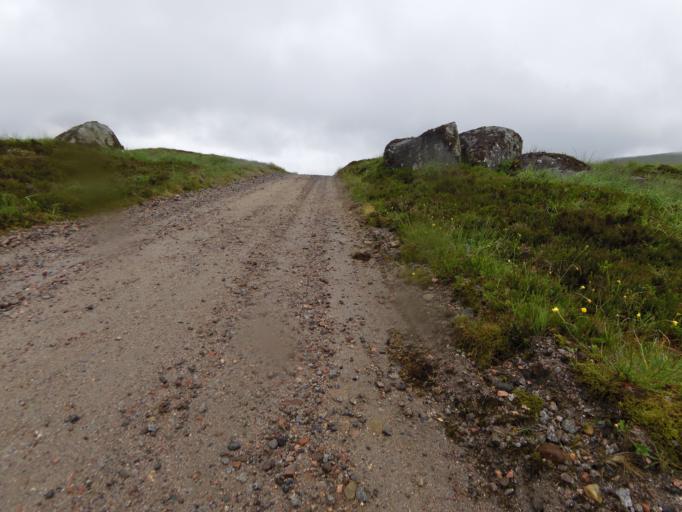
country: GB
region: Scotland
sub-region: Highland
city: Spean Bridge
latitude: 56.7657
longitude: -4.6730
